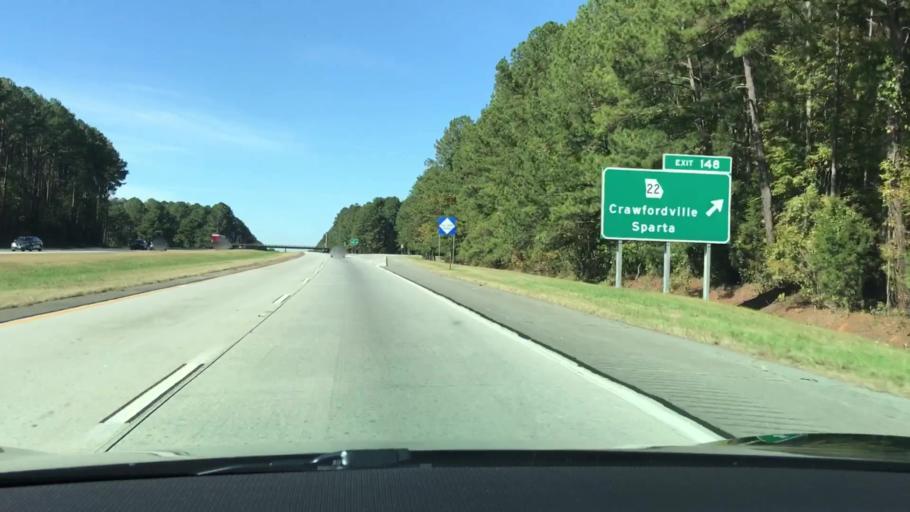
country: US
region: Georgia
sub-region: Taliaferro County
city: Crawfordville
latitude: 33.5296
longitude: -82.9040
